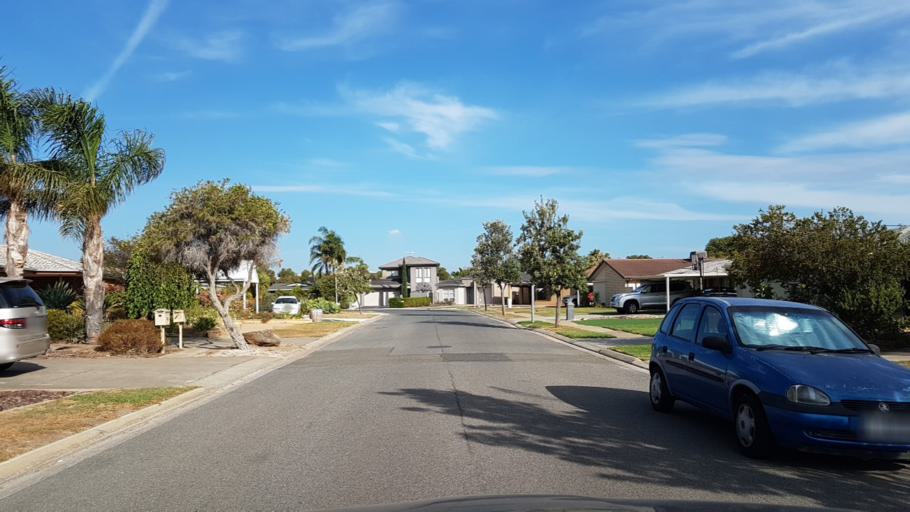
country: AU
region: South Australia
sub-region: Charles Sturt
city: West Lakes Shore
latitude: -34.8614
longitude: 138.4861
